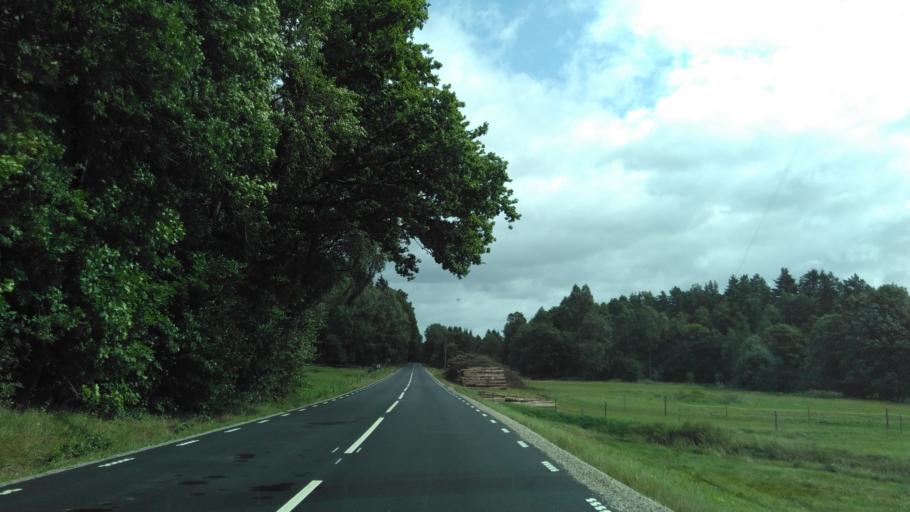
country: SE
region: Vaestra Goetaland
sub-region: Marks Kommun
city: Fritsla
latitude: 57.6038
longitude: 12.7817
